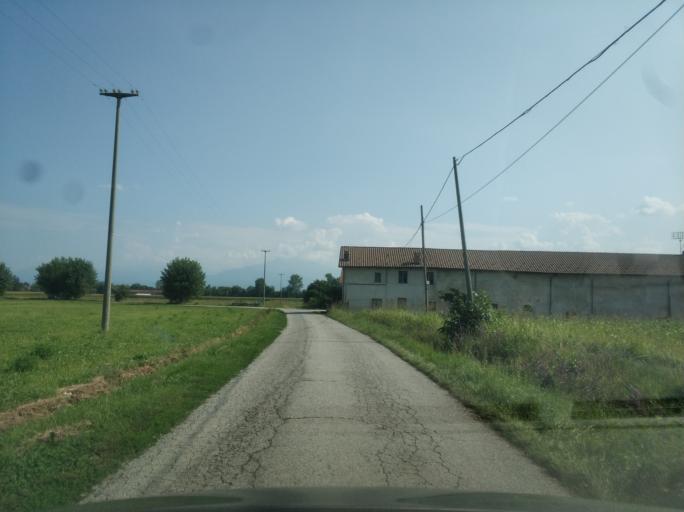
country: IT
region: Piedmont
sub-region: Provincia di Cuneo
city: Roata Rossi
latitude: 44.4550
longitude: 7.4733
